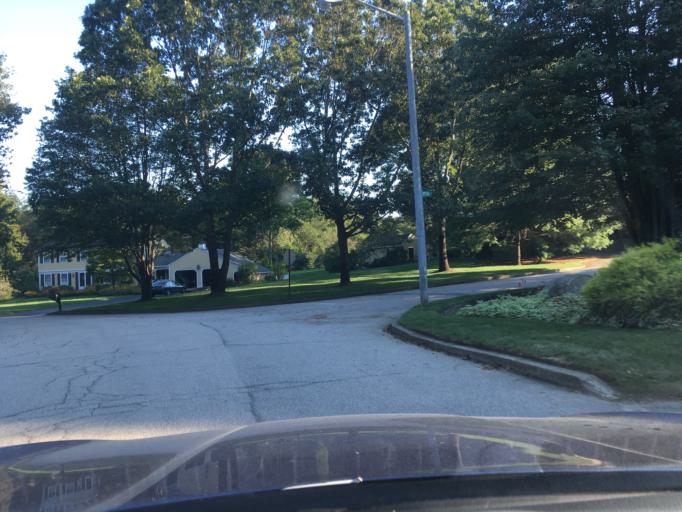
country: US
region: Rhode Island
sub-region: Kent County
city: East Greenwich
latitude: 41.6465
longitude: -71.5023
